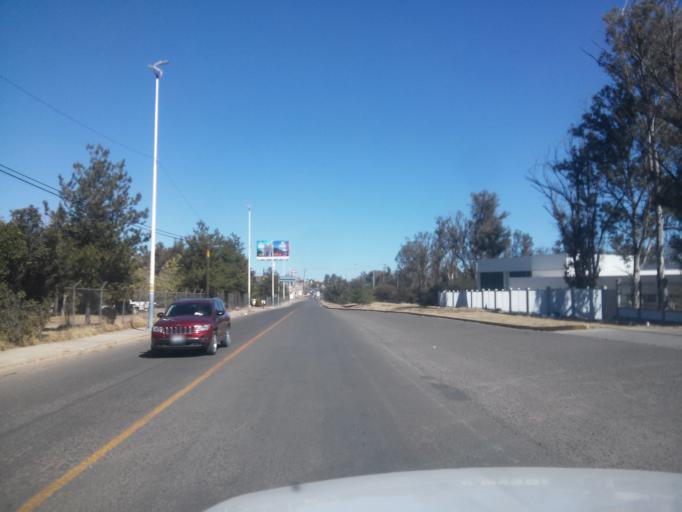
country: MX
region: Durango
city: Victoria de Durango
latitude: 24.0255
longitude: -104.6926
